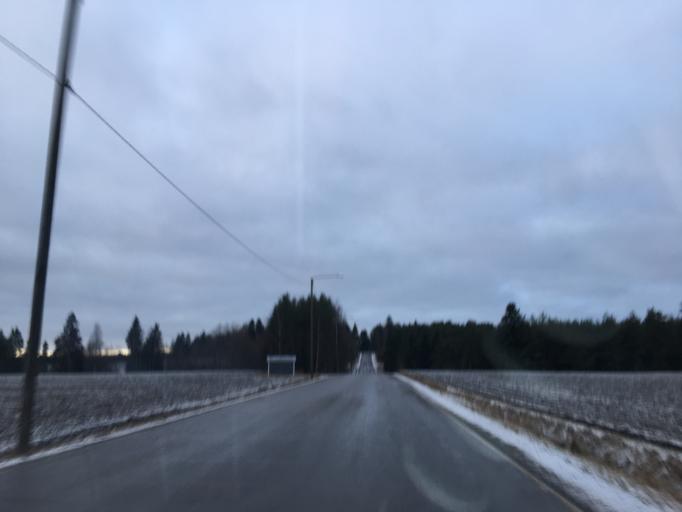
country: FI
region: Varsinais-Suomi
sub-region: Loimaa
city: Aura
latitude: 60.6035
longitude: 22.5487
